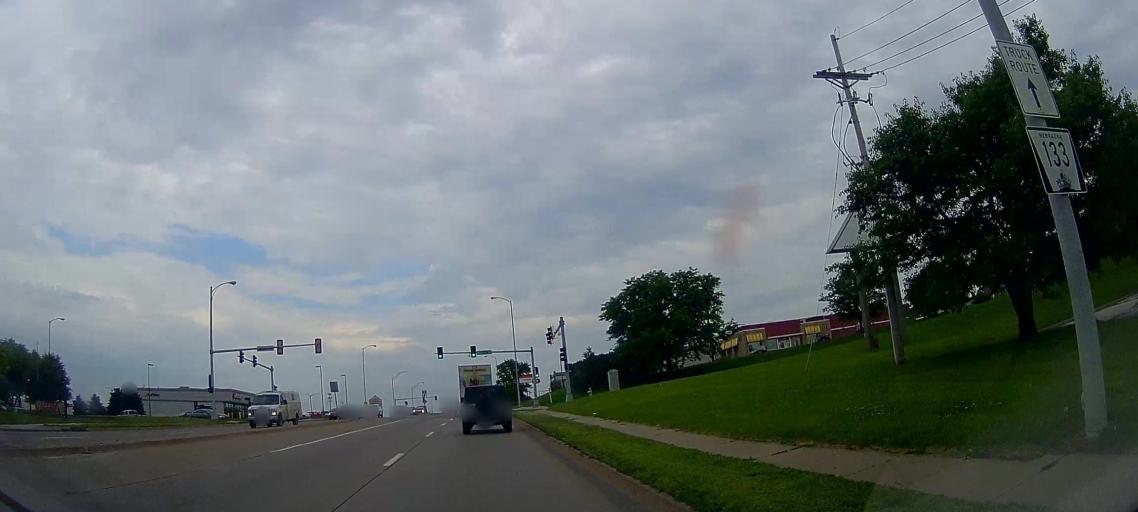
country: US
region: Nebraska
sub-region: Douglas County
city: Ralston
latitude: 41.3114
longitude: -96.0527
